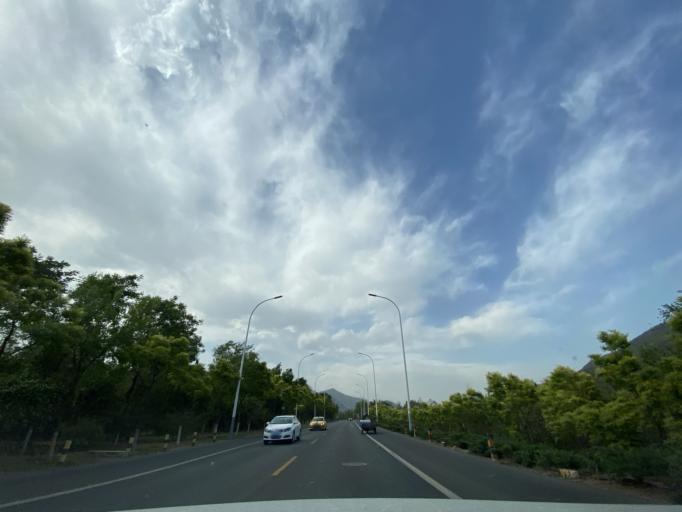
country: CN
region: Beijing
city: Chengzi
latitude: 39.9724
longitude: 116.0854
